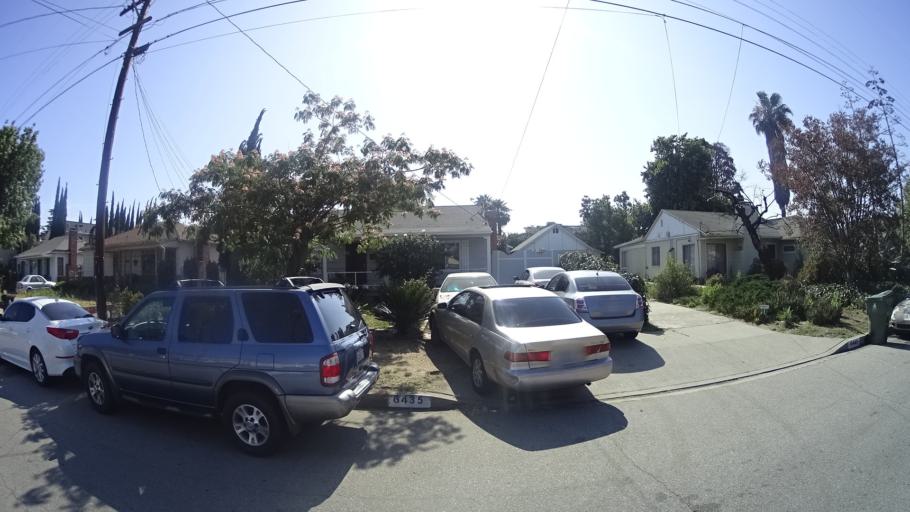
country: US
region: California
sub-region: Los Angeles County
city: Van Nuys
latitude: 34.1877
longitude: -118.4247
